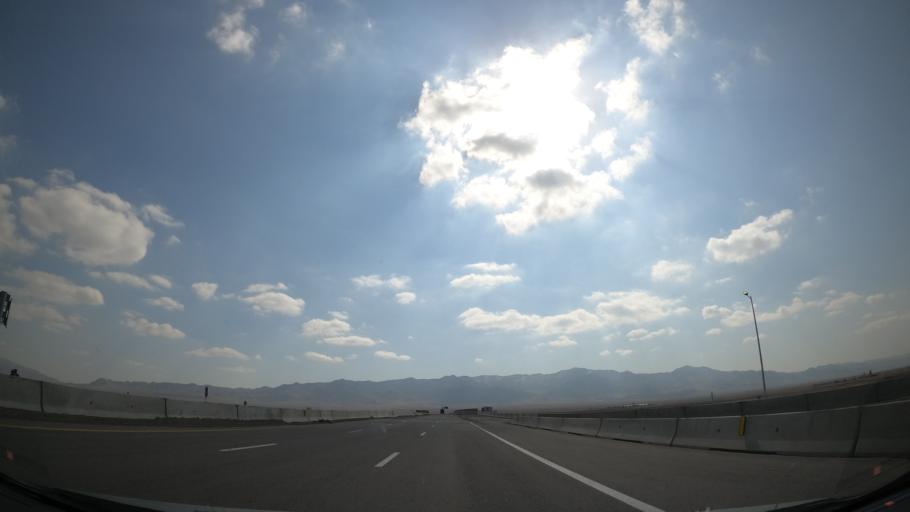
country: IR
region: Alborz
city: Eshtehard
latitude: 35.7400
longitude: 50.5610
